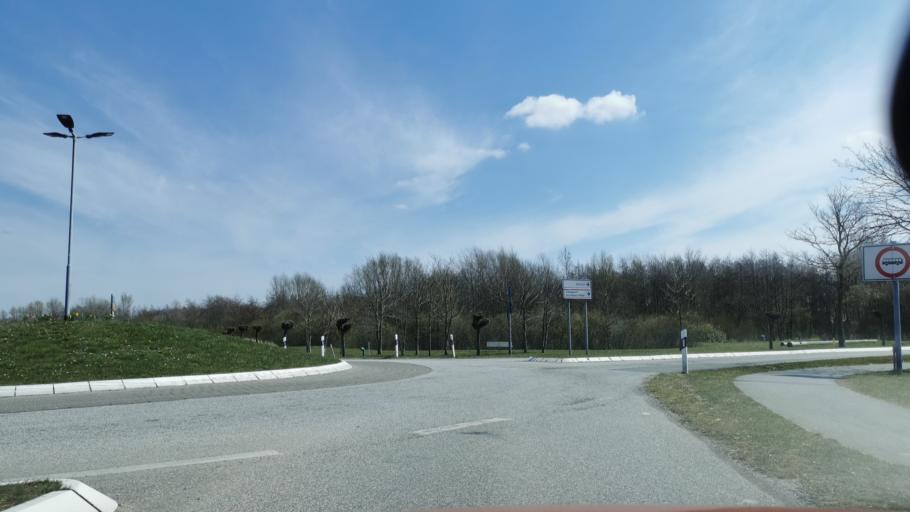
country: DE
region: Schleswig-Holstein
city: Busum
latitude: 54.1413
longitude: 8.8514
